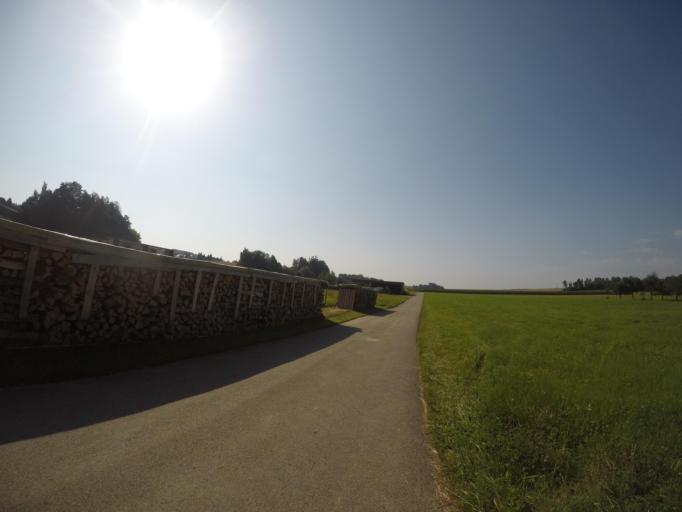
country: DE
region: Baden-Wuerttemberg
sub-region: Tuebingen Region
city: Wain
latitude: 48.2113
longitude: 10.0150
